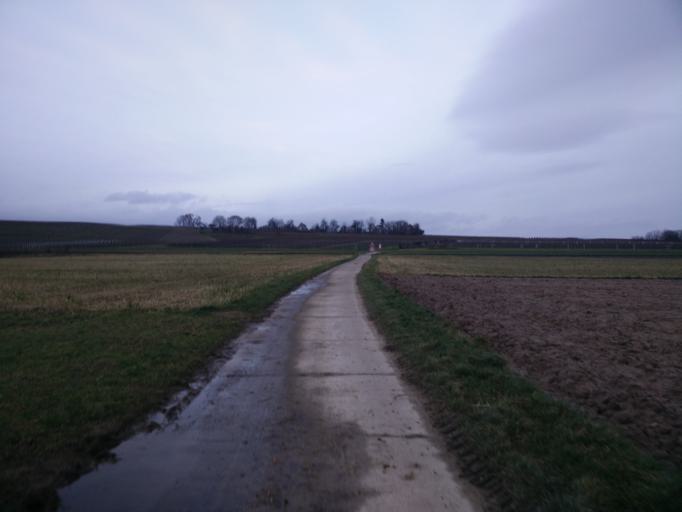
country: DE
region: Rheinland-Pfalz
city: Oberhausen
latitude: 49.1030
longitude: 8.0546
